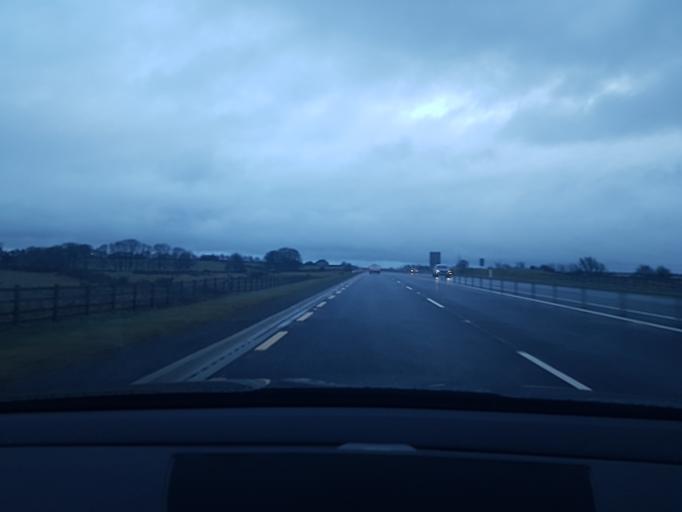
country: IE
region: Connaught
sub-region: County Galway
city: Tuam
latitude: 53.5285
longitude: -8.8671
